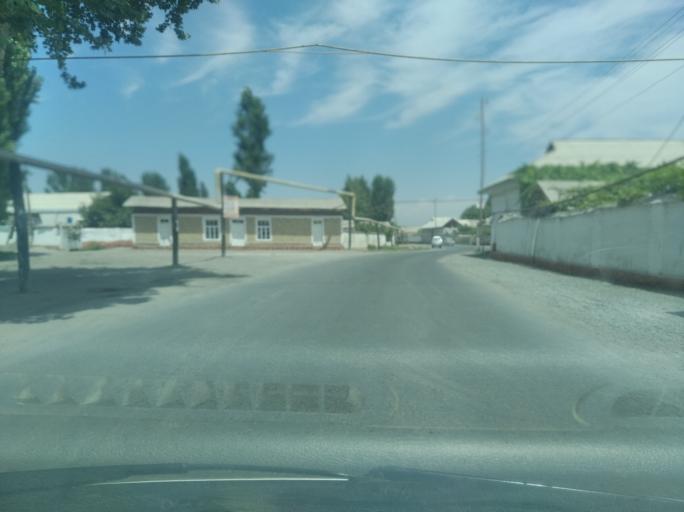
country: UZ
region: Andijon
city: Khujaobod
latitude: 40.6331
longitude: 72.4492
